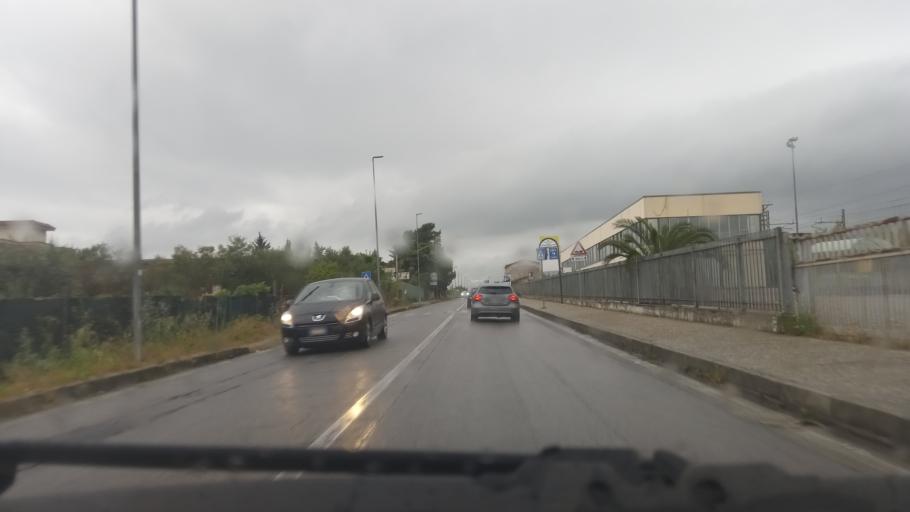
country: IT
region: Latium
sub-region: Provincia di Latina
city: Penitro
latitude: 41.2640
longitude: 13.6734
